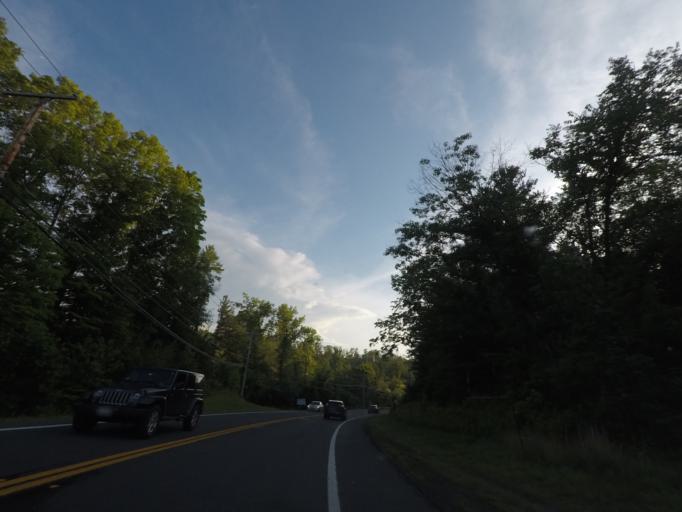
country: US
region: Massachusetts
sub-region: Hampden County
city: Brimfield
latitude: 42.1145
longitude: -72.2259
